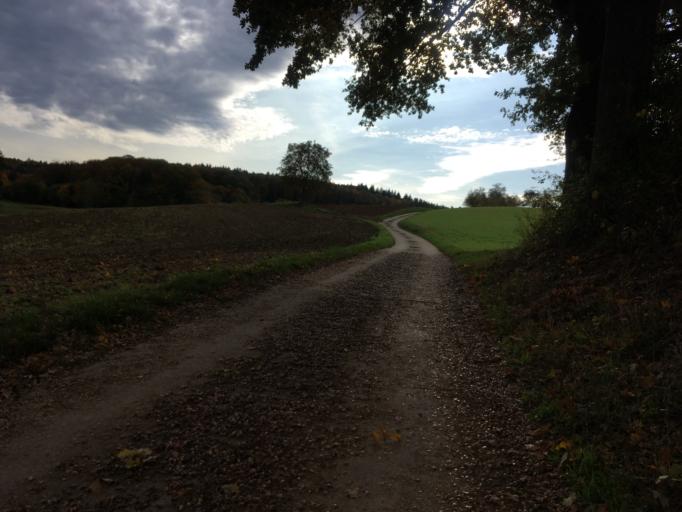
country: DE
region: Baden-Wuerttemberg
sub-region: Karlsruhe Region
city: Neckarbischofsheim
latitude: 49.2830
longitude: 8.9451
